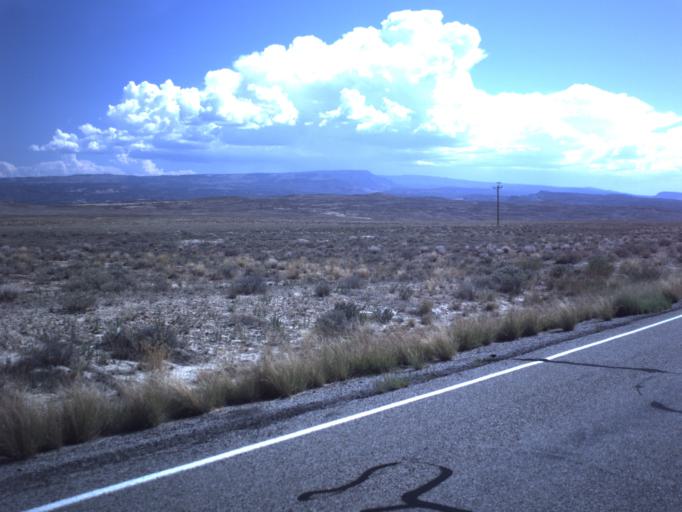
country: US
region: Utah
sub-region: Grand County
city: Moab
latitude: 38.9183
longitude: -109.3325
